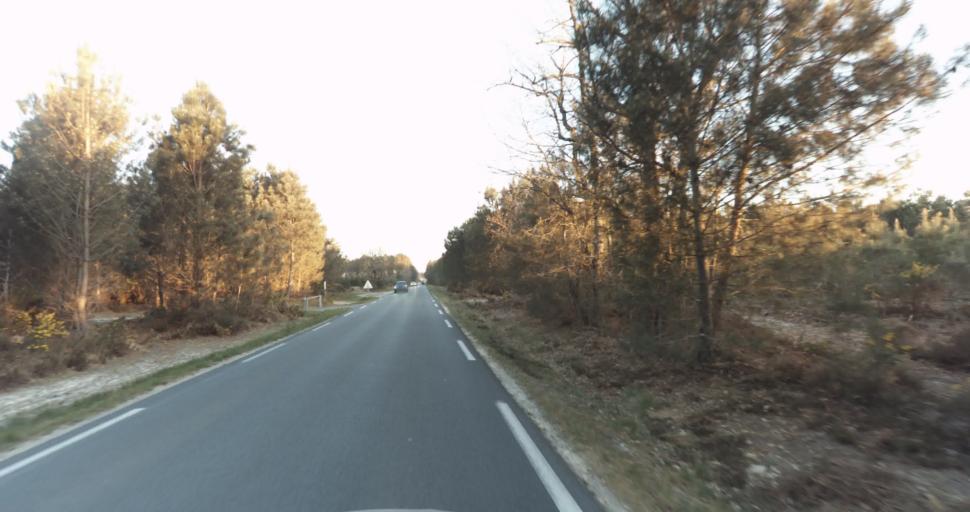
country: FR
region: Aquitaine
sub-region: Departement de la Gironde
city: Martignas-sur-Jalle
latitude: 44.8274
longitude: -0.7626
